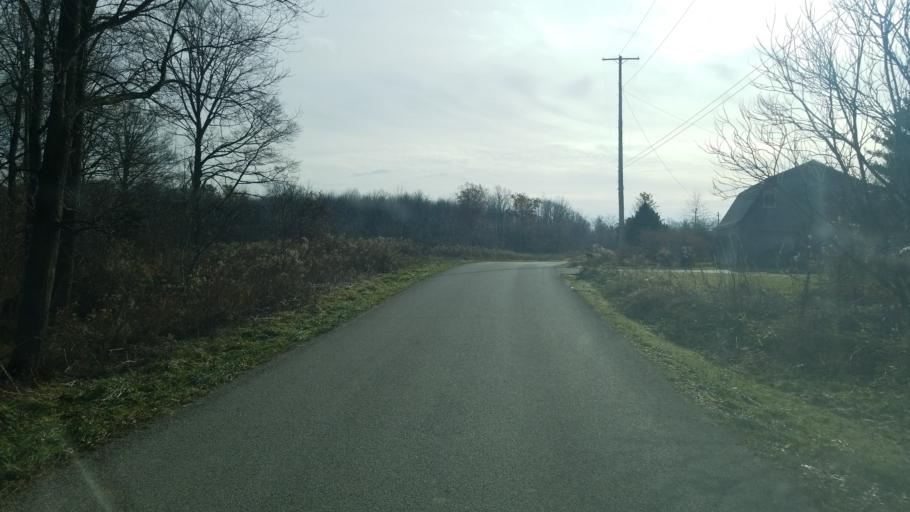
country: US
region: Ohio
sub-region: Ashtabula County
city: Roaming Shores
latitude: 41.6699
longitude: -80.9249
